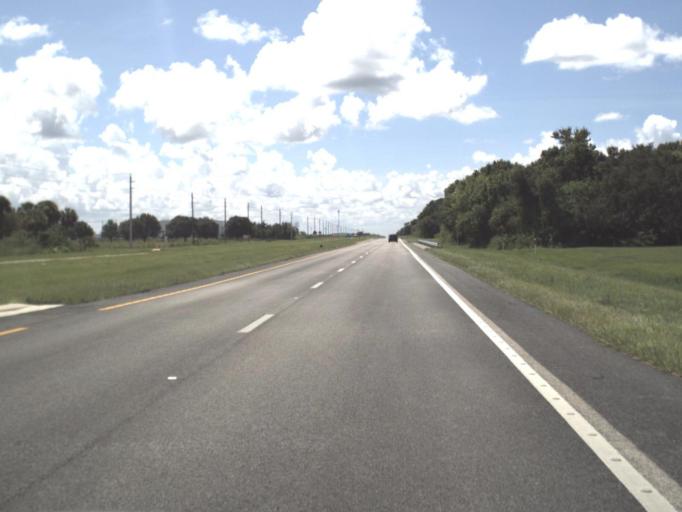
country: US
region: Florida
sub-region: Charlotte County
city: Harbour Heights
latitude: 27.0549
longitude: -81.9585
